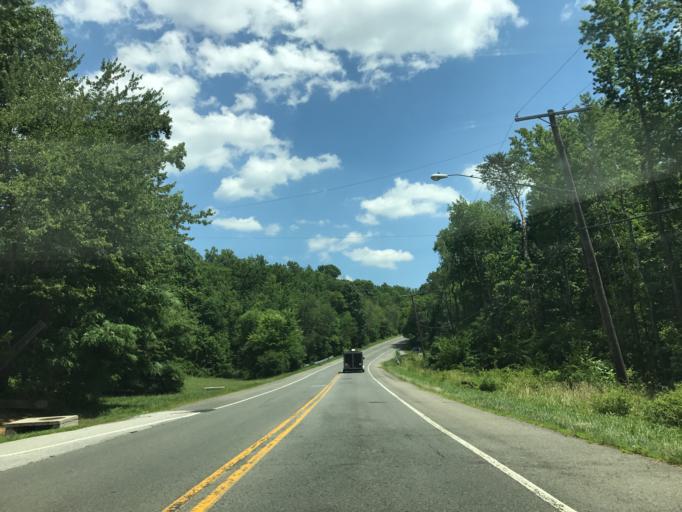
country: US
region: Maryland
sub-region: Prince George's County
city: South Laurel
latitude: 39.0588
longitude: -76.8782
